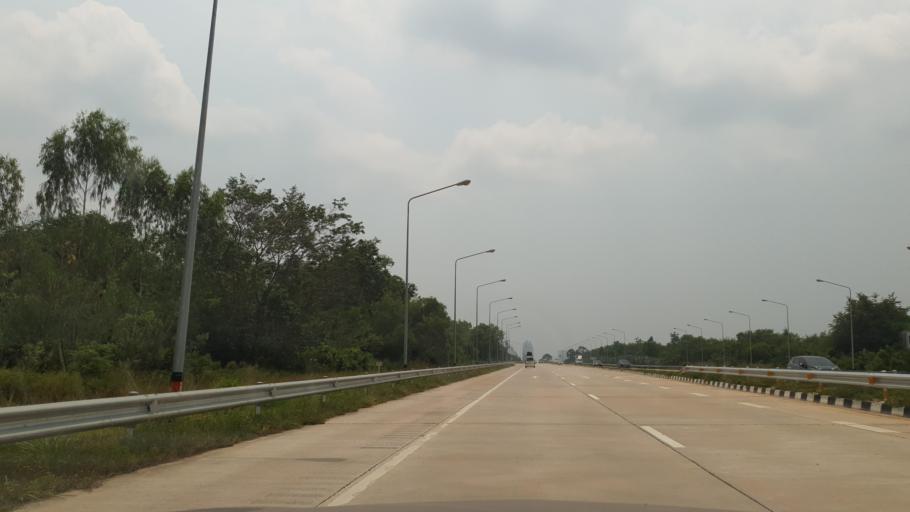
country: TH
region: Chon Buri
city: Phatthaya
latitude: 12.8397
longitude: 100.9514
